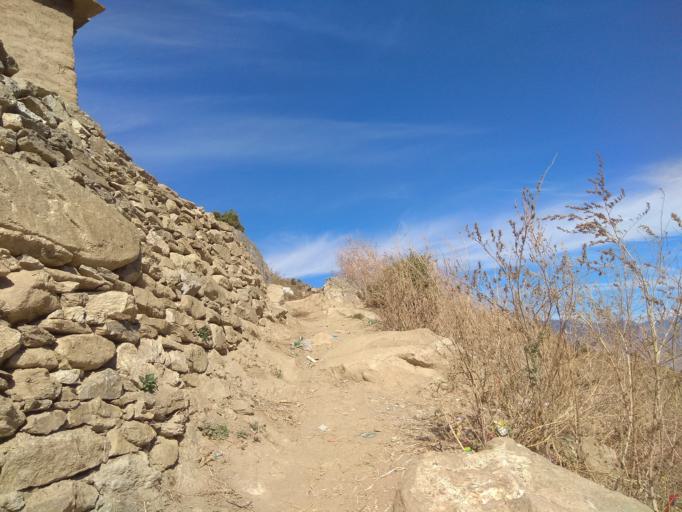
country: NP
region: Mid Western
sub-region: Bheri Zone
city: Dailekh
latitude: 29.2965
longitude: 81.7213
